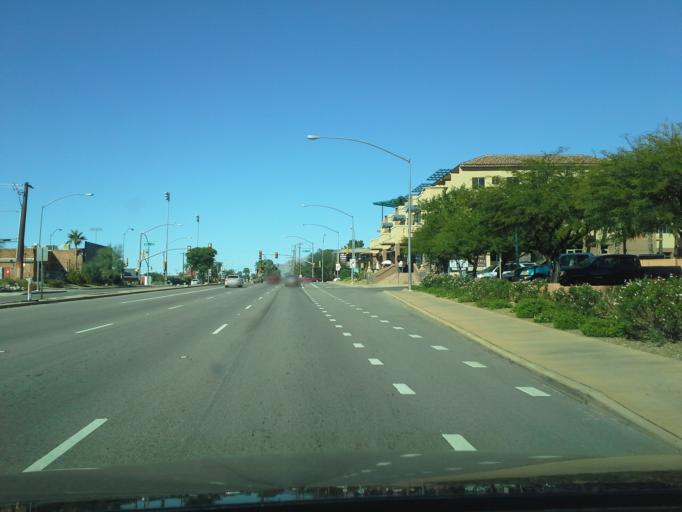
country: US
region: Arizona
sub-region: Pima County
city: Tucson
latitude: 32.2265
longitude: -110.9438
